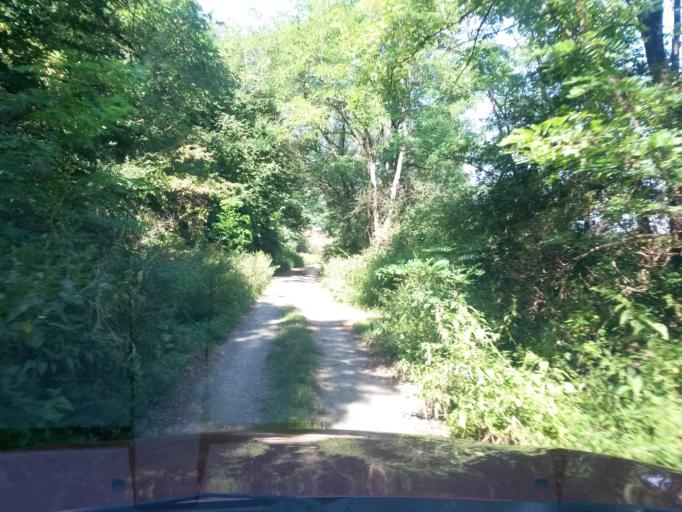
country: HU
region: Borsod-Abauj-Zemplen
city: Gonc
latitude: 48.5247
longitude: 21.1956
